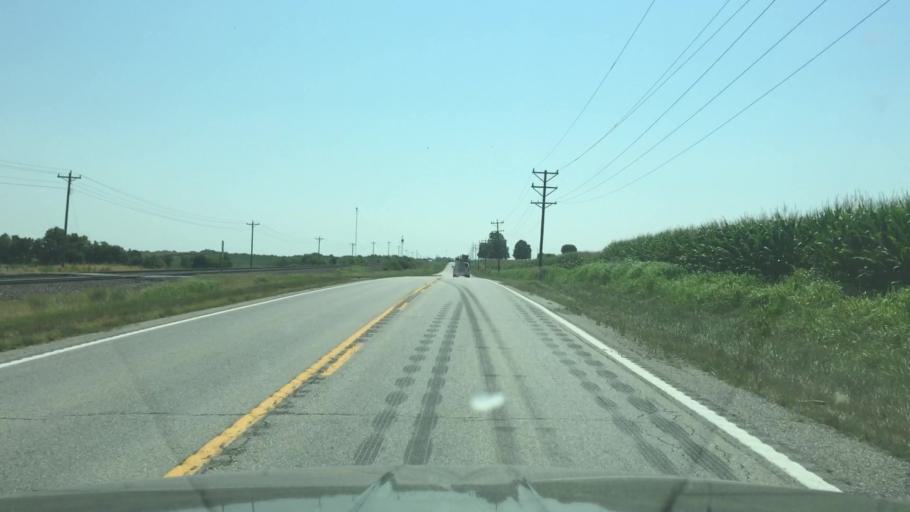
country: US
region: Missouri
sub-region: Moniteau County
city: Tipton
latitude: 38.6657
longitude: -92.8343
